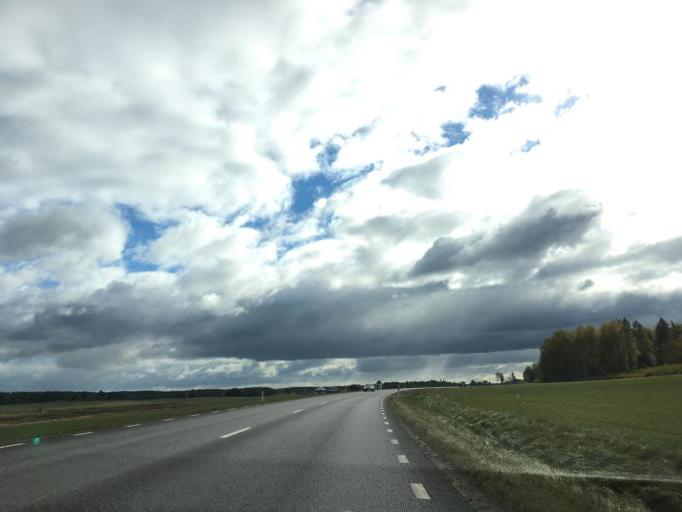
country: SE
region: Soedermanland
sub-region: Katrineholms Kommun
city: Katrineholm
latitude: 58.9657
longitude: 16.3655
